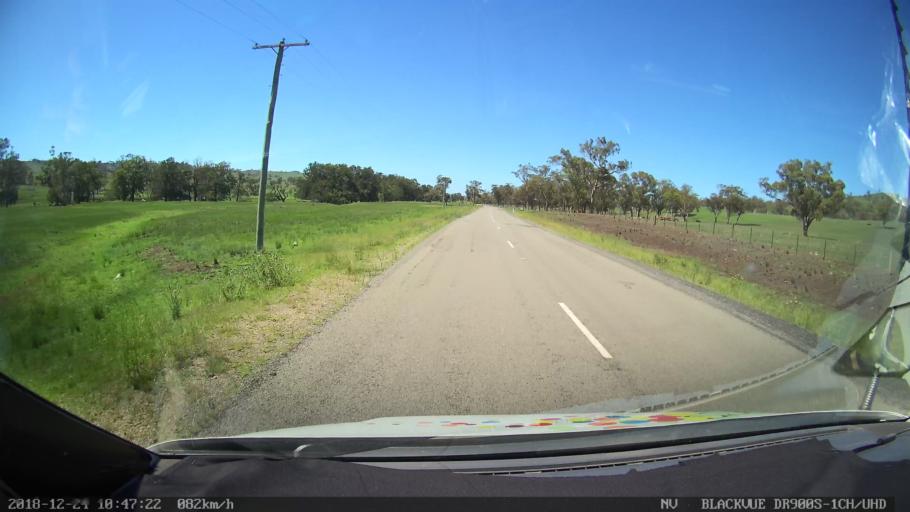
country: AU
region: New South Wales
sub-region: Upper Hunter Shire
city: Merriwa
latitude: -31.9236
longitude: 150.4296
